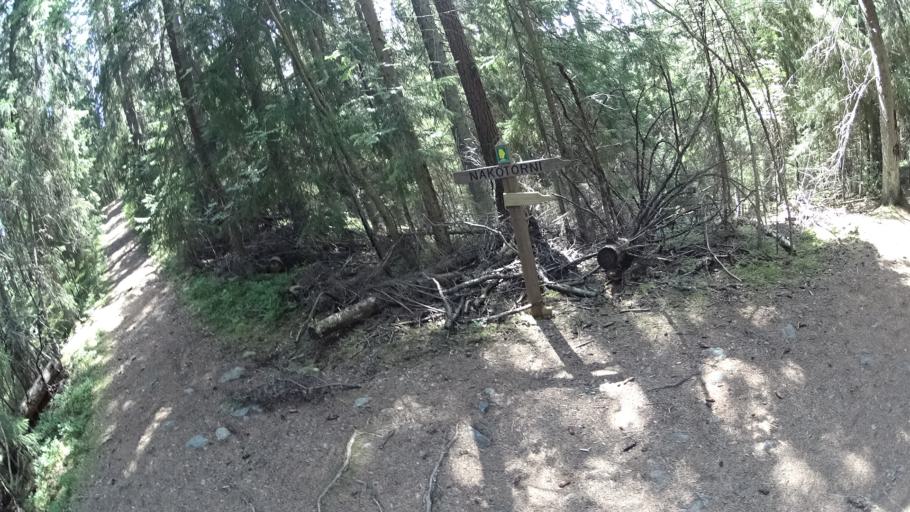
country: FI
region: Haeme
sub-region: Forssa
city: Tammela
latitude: 60.7760
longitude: 23.8377
